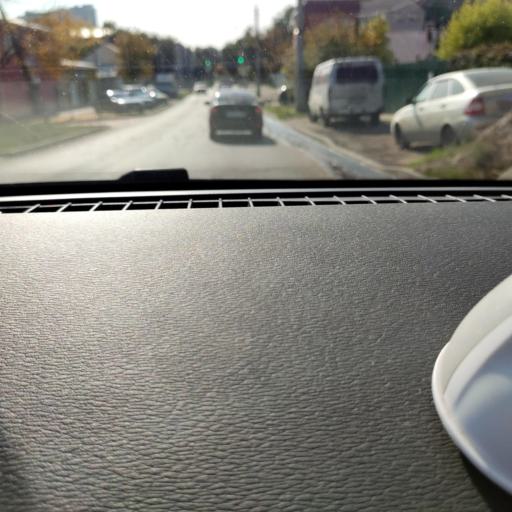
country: RU
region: Samara
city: Samara
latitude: 53.1983
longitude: 50.2038
